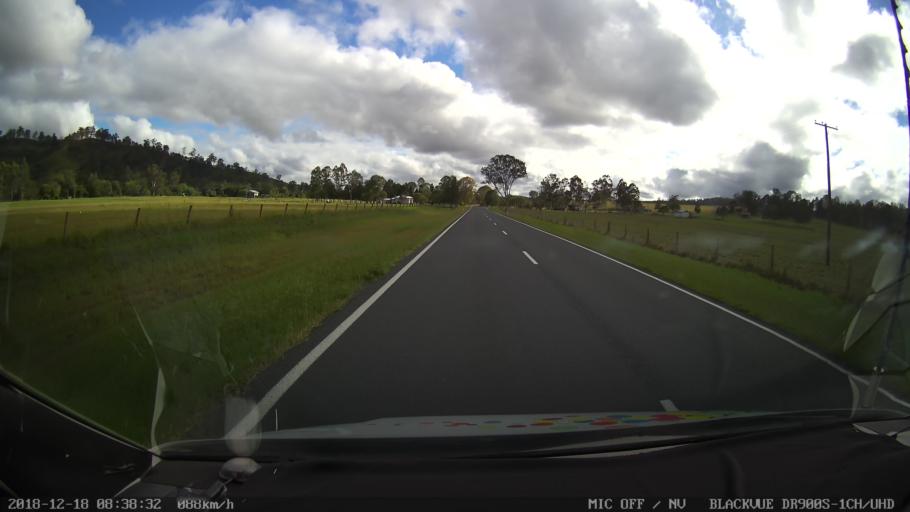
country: AU
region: New South Wales
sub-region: Kyogle
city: Kyogle
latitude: -28.2552
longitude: 152.8287
